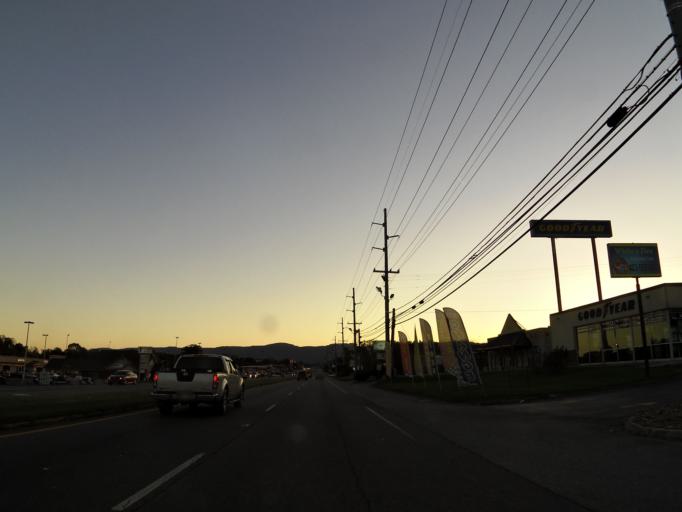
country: US
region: Tennessee
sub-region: Campbell County
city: Hunter
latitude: 36.3491
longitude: -84.1598
